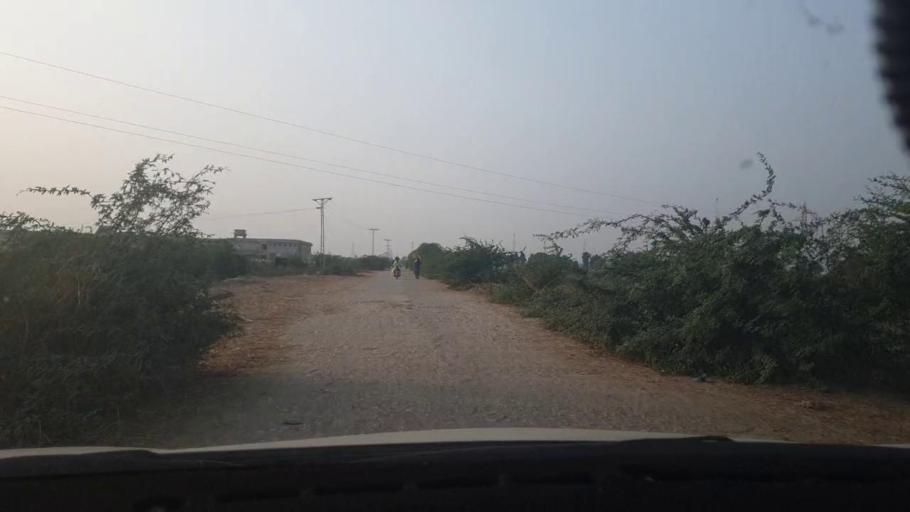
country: PK
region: Sindh
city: Bulri
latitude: 24.8535
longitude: 68.3403
